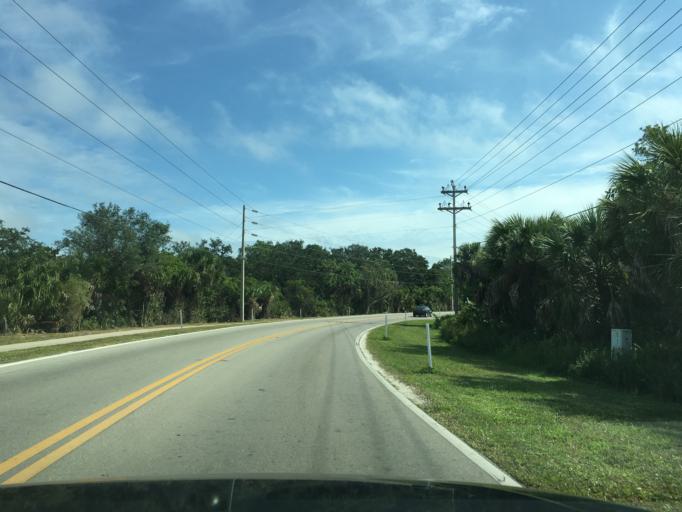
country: US
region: Florida
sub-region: Lee County
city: Saint James City
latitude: 26.4509
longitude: -82.1276
